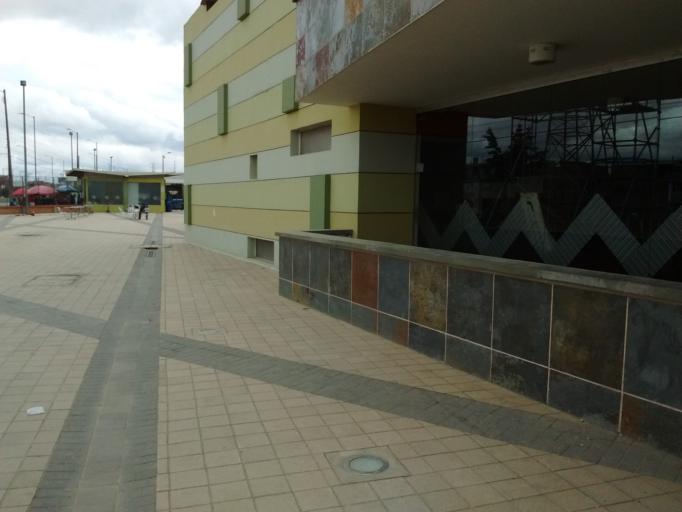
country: CO
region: Cundinamarca
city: Soacha
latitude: 4.5926
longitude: -74.1915
